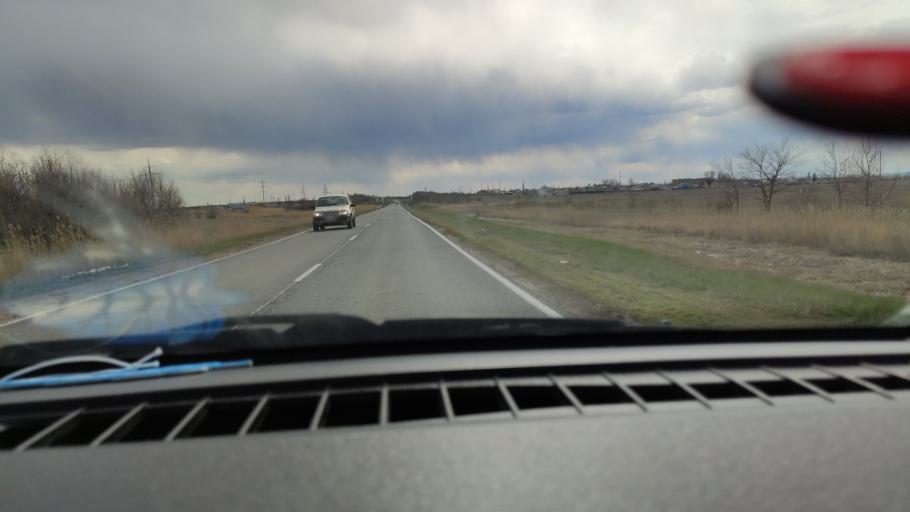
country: RU
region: Saratov
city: Privolzhskiy
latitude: 51.3032
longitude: 46.0039
